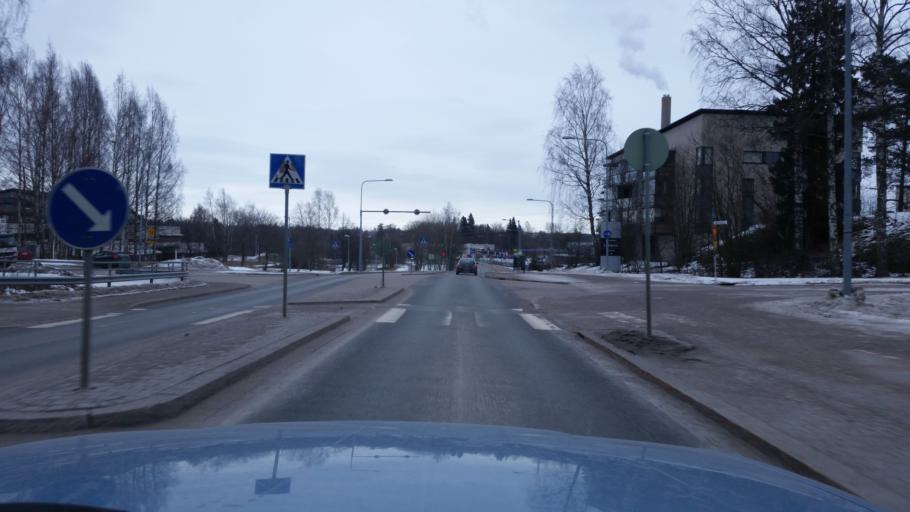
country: FI
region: Uusimaa
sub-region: Helsinki
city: Helsinki
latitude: 60.2355
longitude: 24.9709
